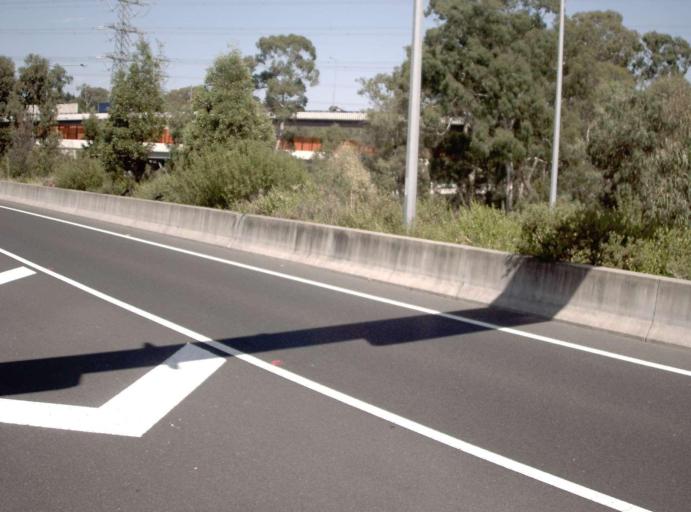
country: AU
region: Victoria
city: Mitcham
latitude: -37.8126
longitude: 145.2176
